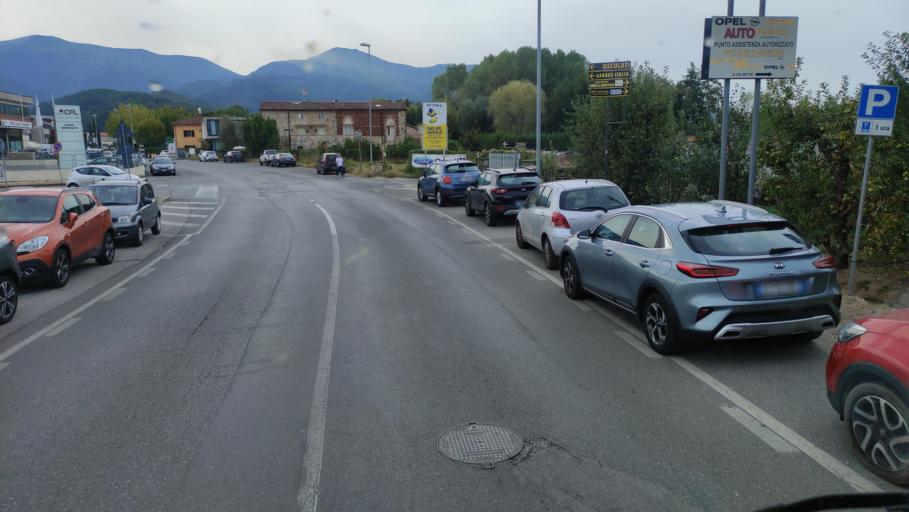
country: IT
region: Tuscany
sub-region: Provincia di Lucca
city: Lucca
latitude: 43.8141
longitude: 10.4974
